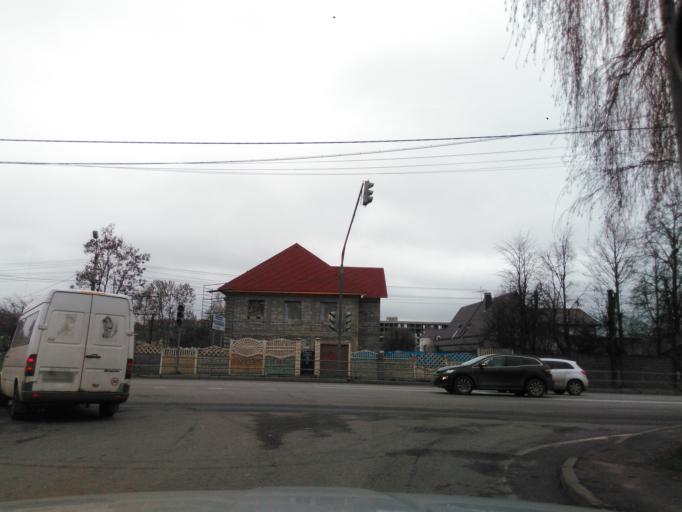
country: RU
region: Moskovskaya
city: Nakhabino
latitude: 55.8474
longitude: 37.1896
